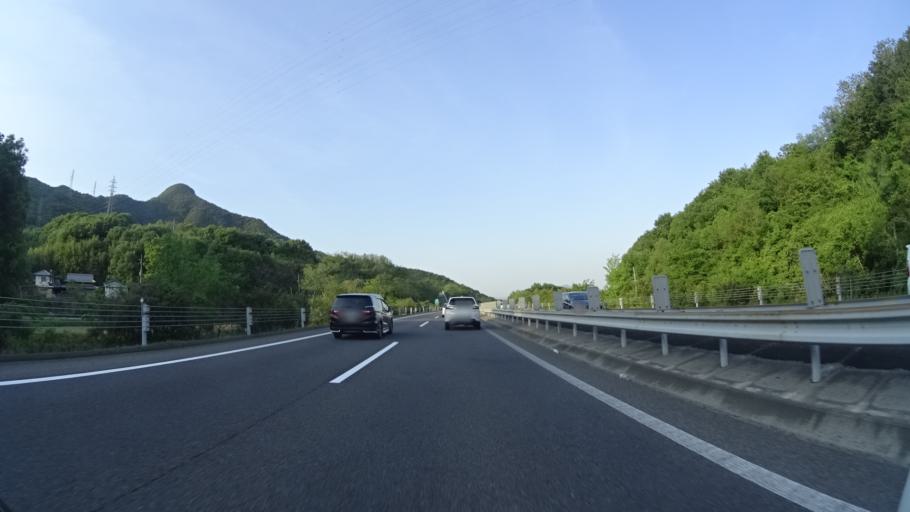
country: JP
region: Kagawa
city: Tadotsu
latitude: 34.2244
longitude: 133.7332
